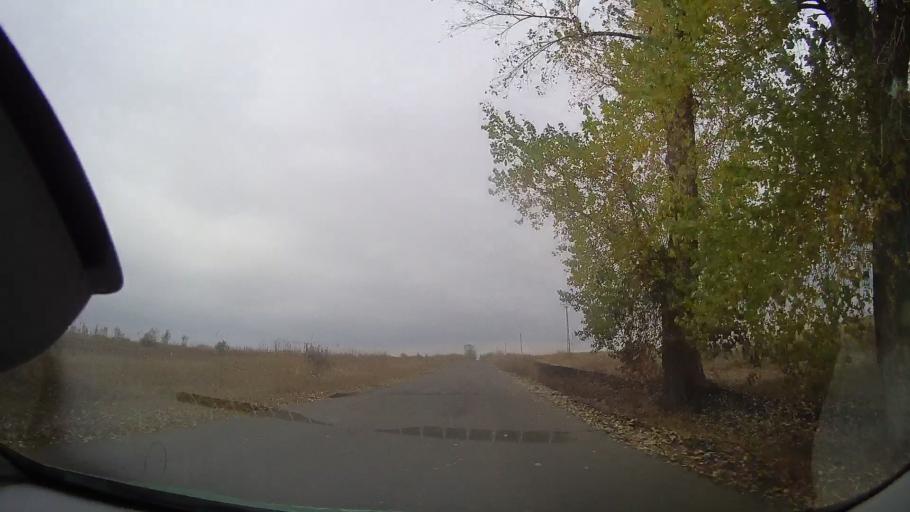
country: RO
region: Braila
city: Dudesti
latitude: 44.9351
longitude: 27.4259
